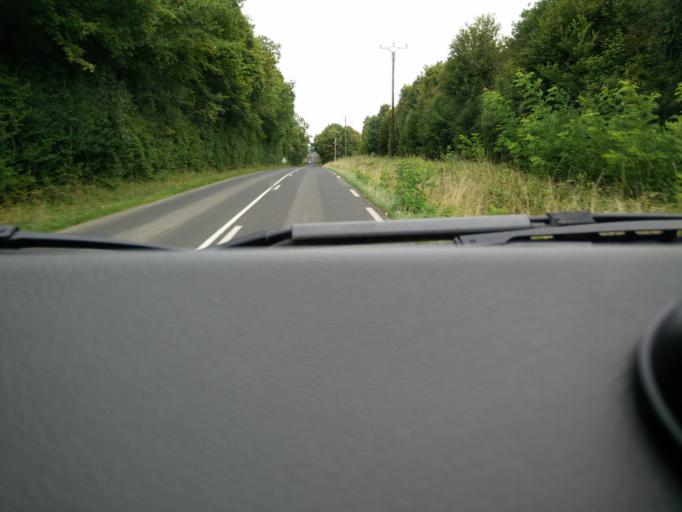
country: FR
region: Lorraine
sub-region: Departement de Meurthe-et-Moselle
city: Montauville
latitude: 48.9183
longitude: 5.9169
